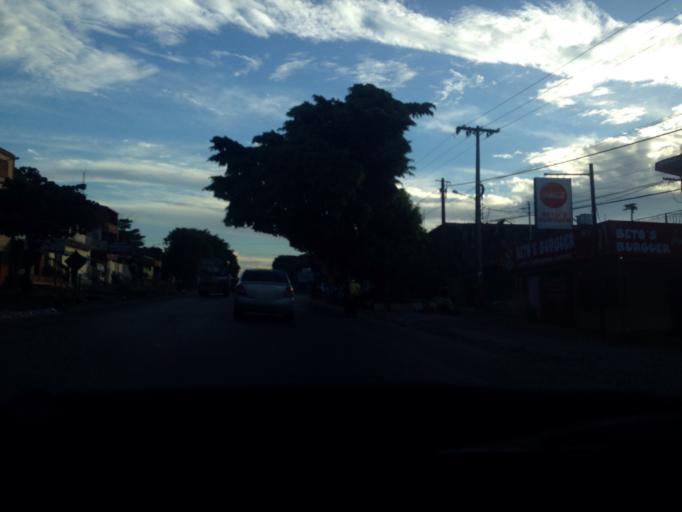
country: PY
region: Central
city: Lambare
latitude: -25.3465
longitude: -57.5891
